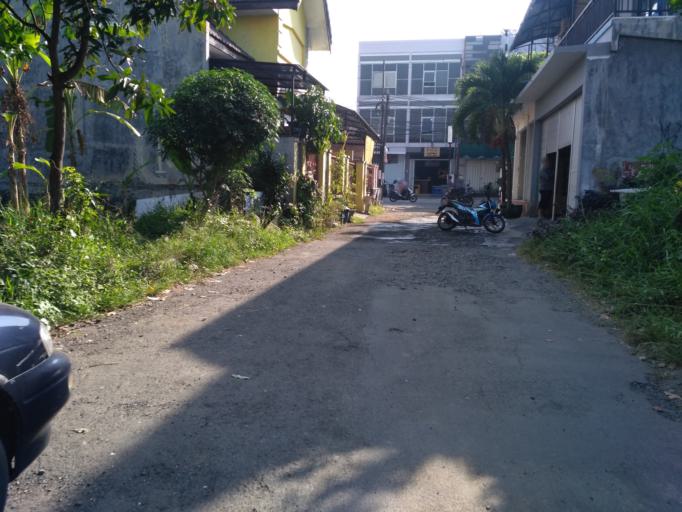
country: ID
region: East Java
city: Malang
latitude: -7.9470
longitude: 112.6229
